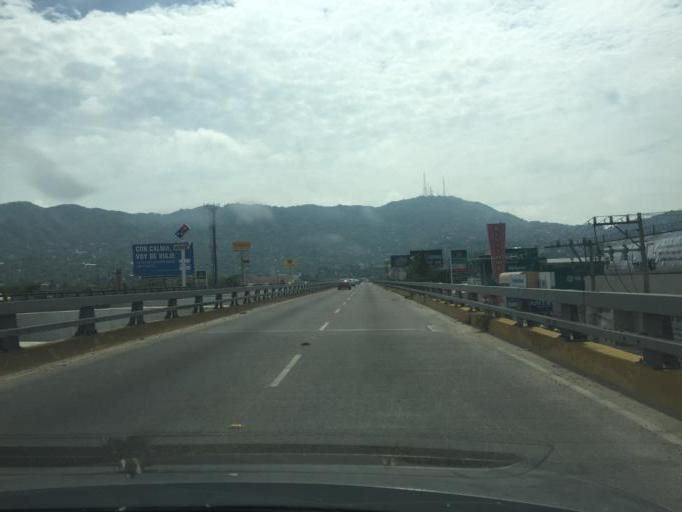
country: MX
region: Guerrero
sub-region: Acapulco de Juarez
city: Nueva Frontera
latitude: 16.8945
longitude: -99.8333
